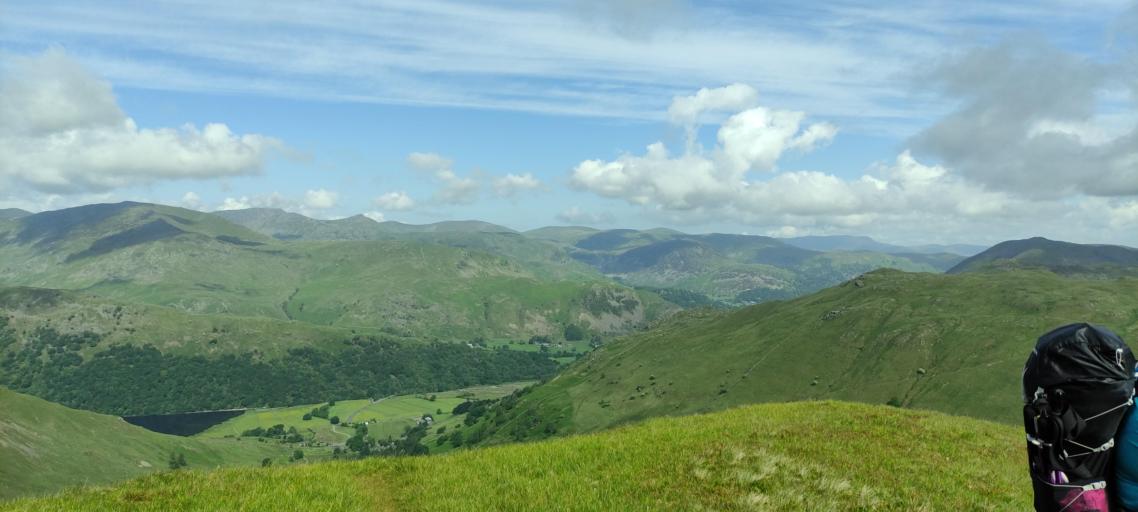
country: GB
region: England
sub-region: Cumbria
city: Ambleside
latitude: 54.5031
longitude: -2.8902
